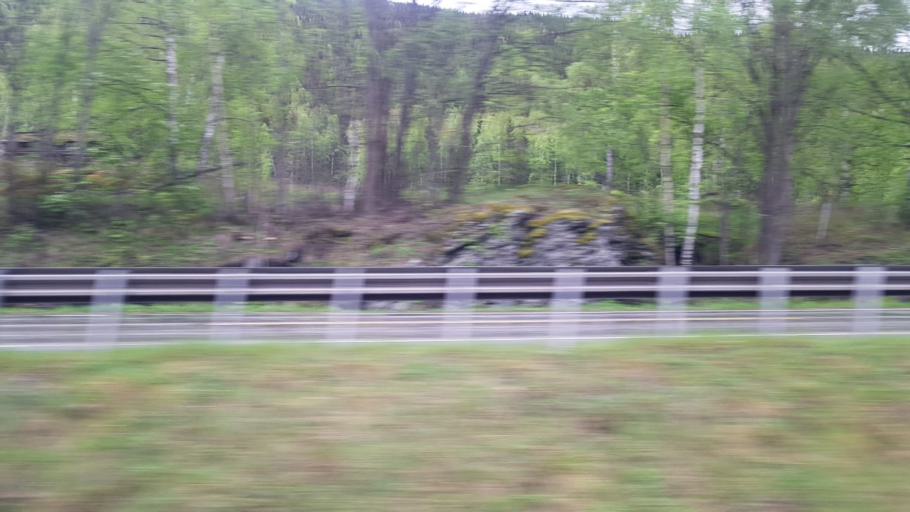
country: NO
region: Oppland
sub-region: Nord-Fron
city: Vinstra
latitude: 61.6189
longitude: 9.7127
